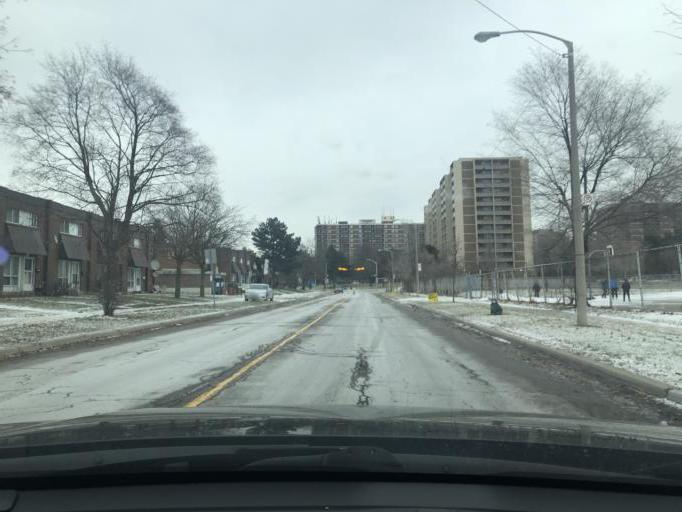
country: CA
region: Ontario
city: Scarborough
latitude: 43.7821
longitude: -79.3034
